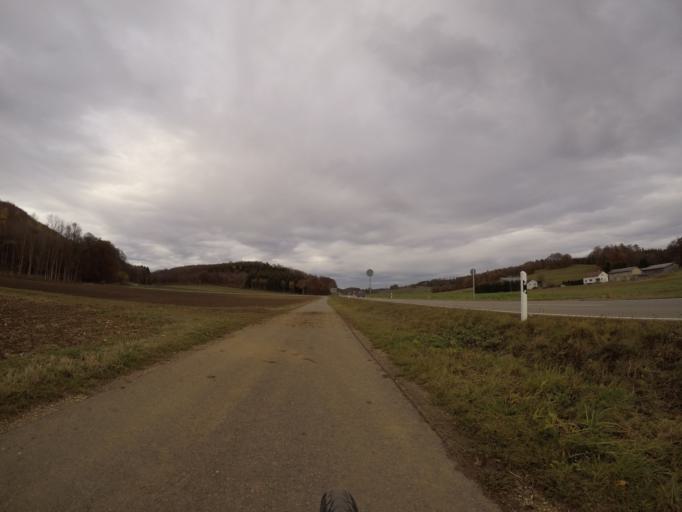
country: DE
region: Baden-Wuerttemberg
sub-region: Tuebingen Region
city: Sankt Johann
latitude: 48.4052
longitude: 9.2859
